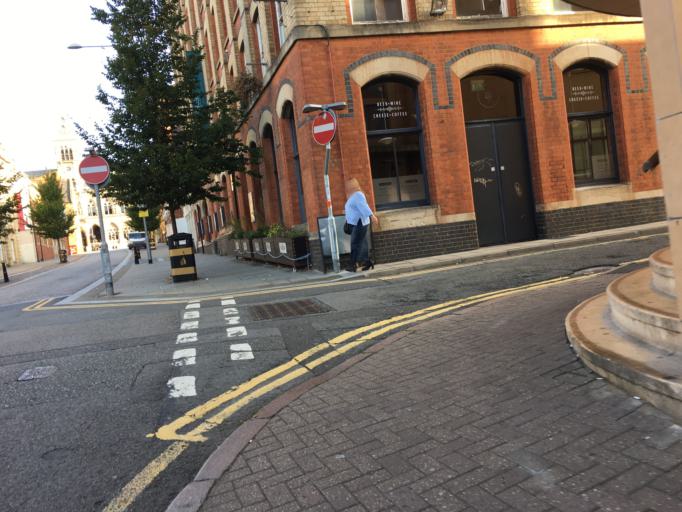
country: GB
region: England
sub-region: Northamptonshire
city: Northampton
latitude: 52.2360
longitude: -0.8942
